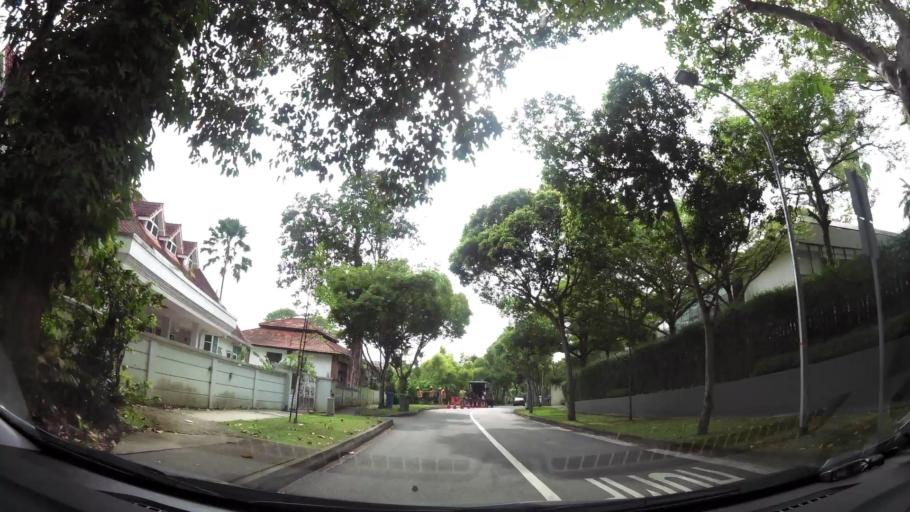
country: SG
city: Singapore
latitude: 1.3168
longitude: 103.7921
